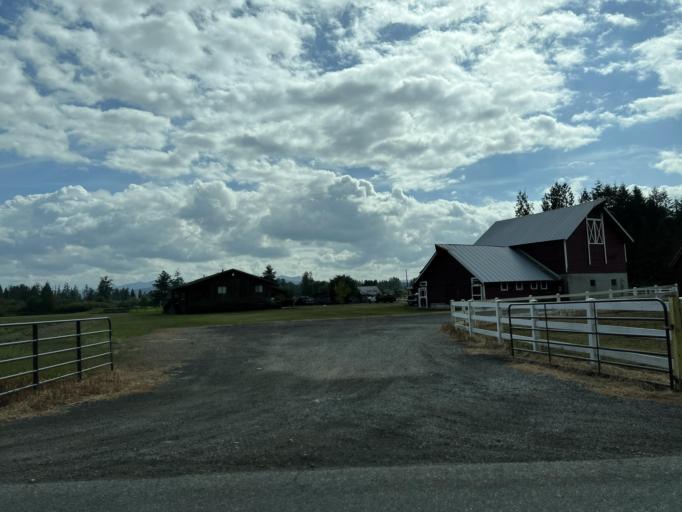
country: US
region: Washington
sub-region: King County
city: Carnation
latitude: 47.6369
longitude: -121.9148
